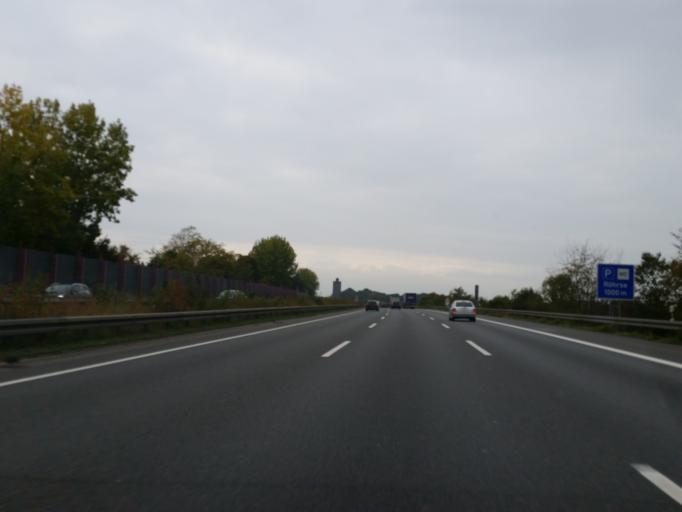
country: DE
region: Lower Saxony
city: Dollbergen
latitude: 52.3570
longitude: 10.1846
